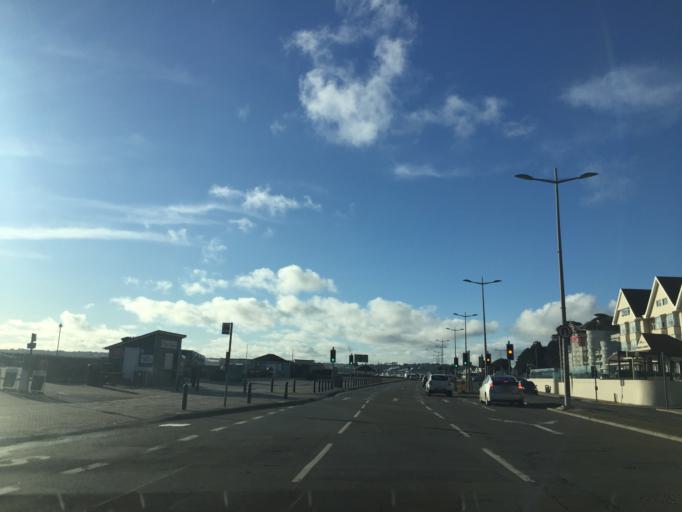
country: JE
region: St Helier
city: Saint Helier
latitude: 49.1867
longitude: -2.1154
